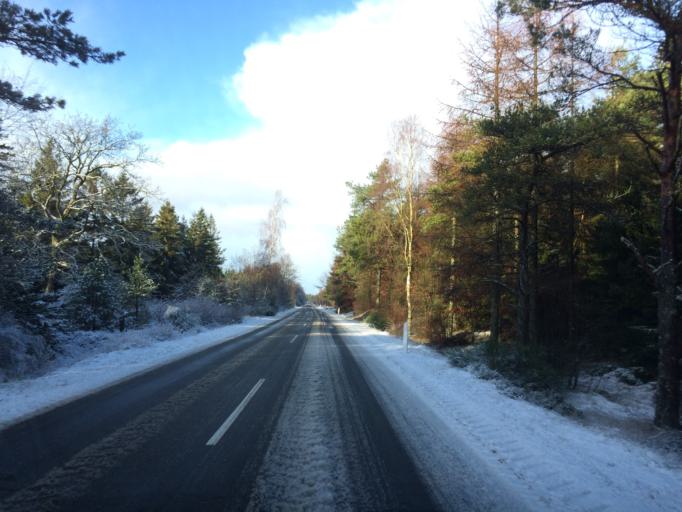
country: DK
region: Central Jutland
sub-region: Holstebro Kommune
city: Ulfborg
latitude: 56.2581
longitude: 8.3519
